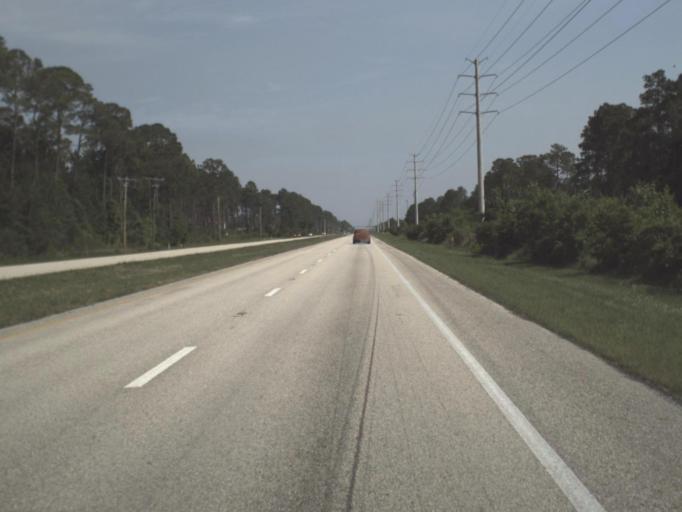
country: US
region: Florida
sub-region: Saint Johns County
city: Villano Beach
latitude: 30.0201
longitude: -81.3991
